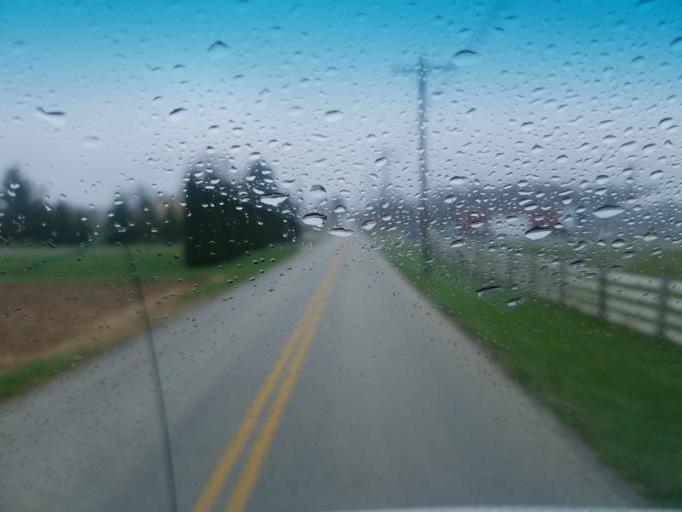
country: US
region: Ohio
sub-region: Wood County
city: North Baltimore
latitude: 41.1471
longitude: -83.6312
